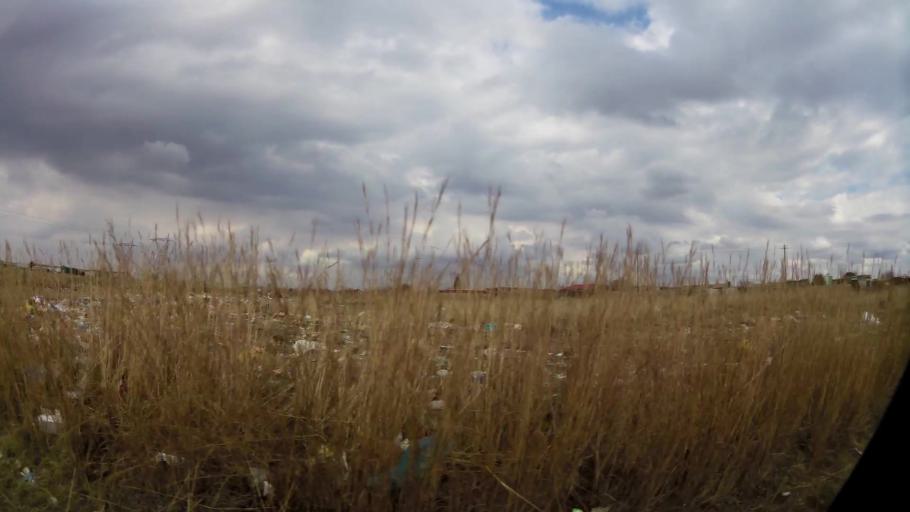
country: ZA
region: Gauteng
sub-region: Sedibeng District Municipality
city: Vanderbijlpark
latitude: -26.6790
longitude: 27.7905
